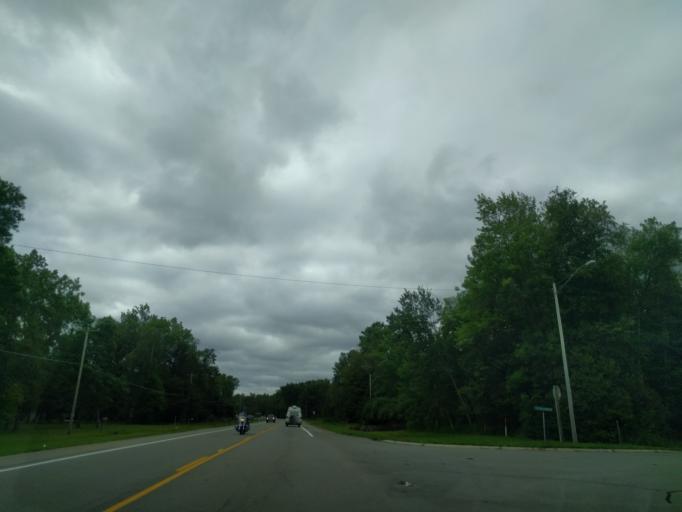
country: US
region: Michigan
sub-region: Menominee County
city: Menominee
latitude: 45.1655
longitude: -87.5879
